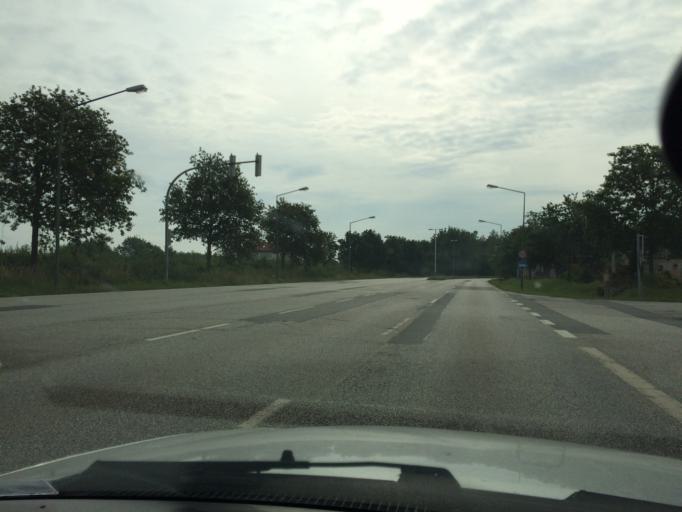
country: DE
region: Schleswig-Holstein
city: Flensburg
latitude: 54.7590
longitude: 9.4379
